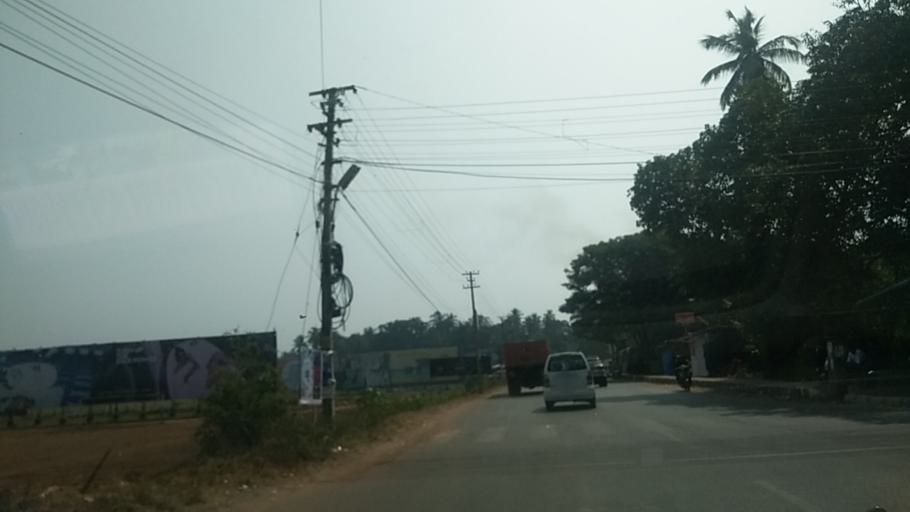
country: IN
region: Goa
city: Calangute
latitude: 15.5674
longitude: 73.7649
